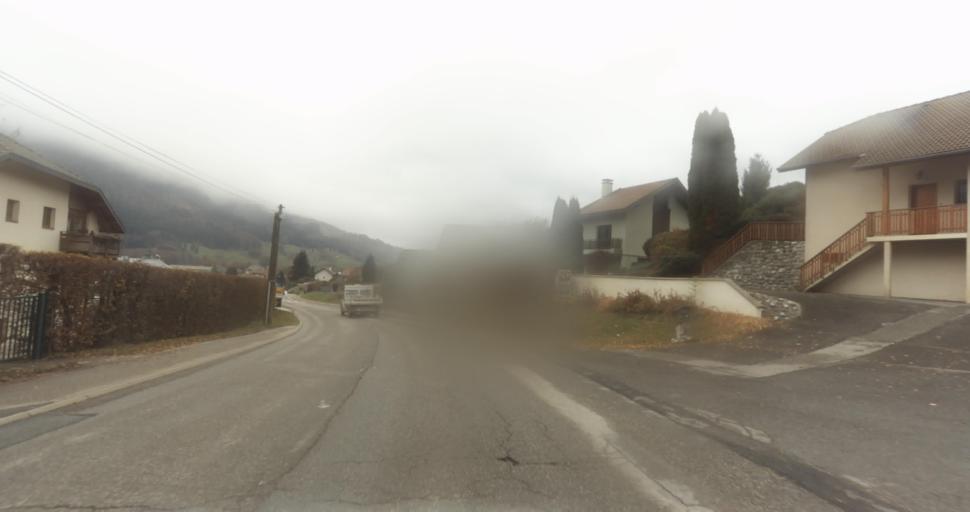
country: FR
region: Rhone-Alpes
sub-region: Departement de la Haute-Savoie
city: Thorens-Glieres
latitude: 46.0006
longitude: 6.2514
